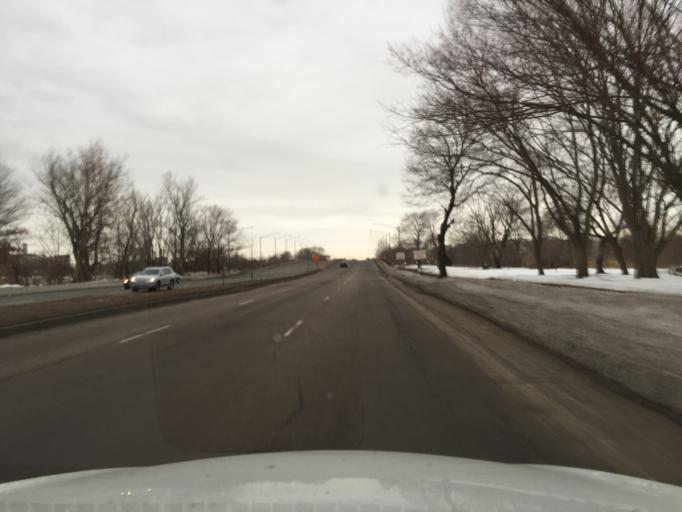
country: US
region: Massachusetts
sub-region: Middlesex County
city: Somerville
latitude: 42.4022
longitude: -71.0829
